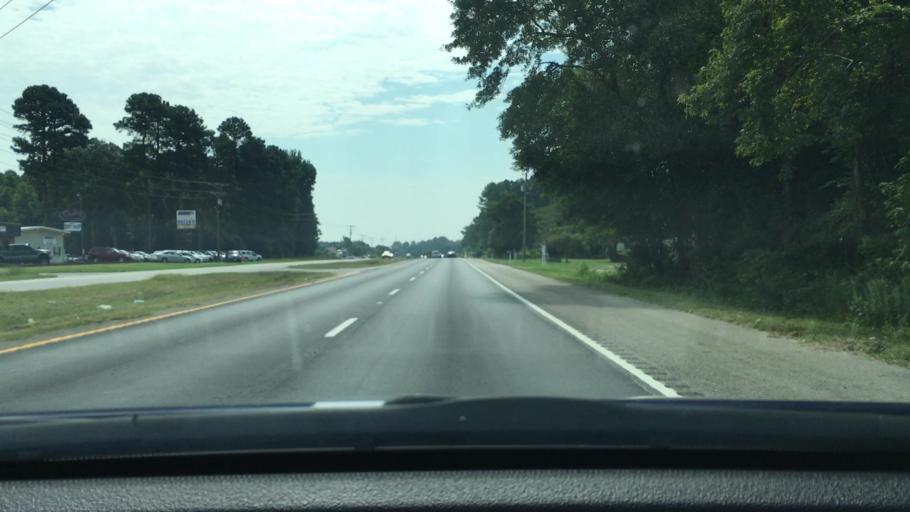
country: US
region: South Carolina
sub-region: Sumter County
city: Cherryvale
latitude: 33.9645
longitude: -80.4375
